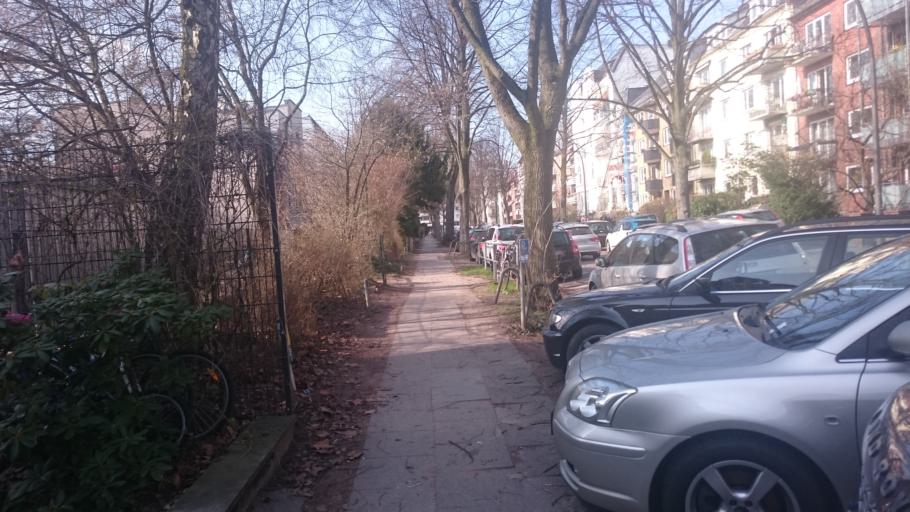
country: DE
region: Hamburg
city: Hamburg-Nord
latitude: 53.5797
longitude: 9.9726
